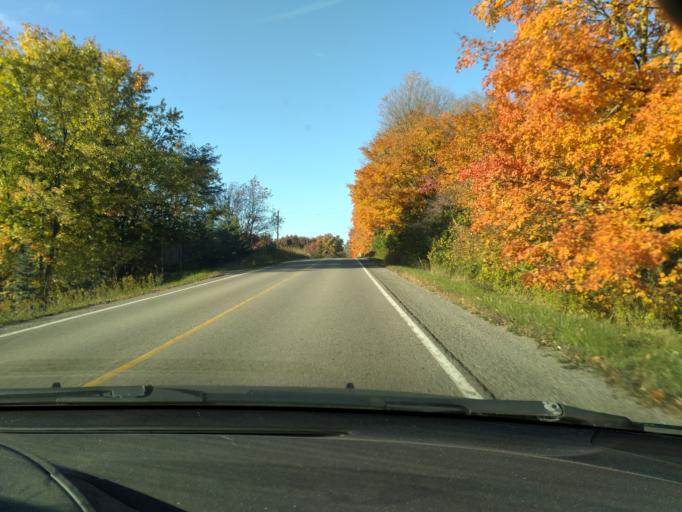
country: CA
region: Ontario
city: Bradford West Gwillimbury
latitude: 43.9567
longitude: -79.7168
